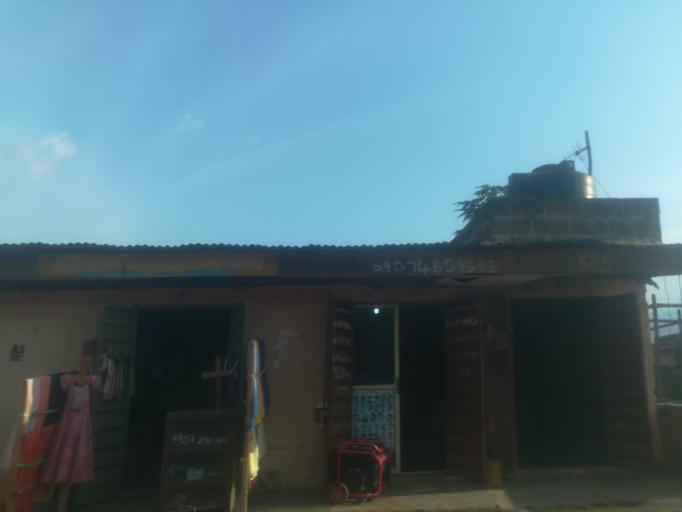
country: NG
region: Oyo
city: Ibadan
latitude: 7.3803
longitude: 3.8093
